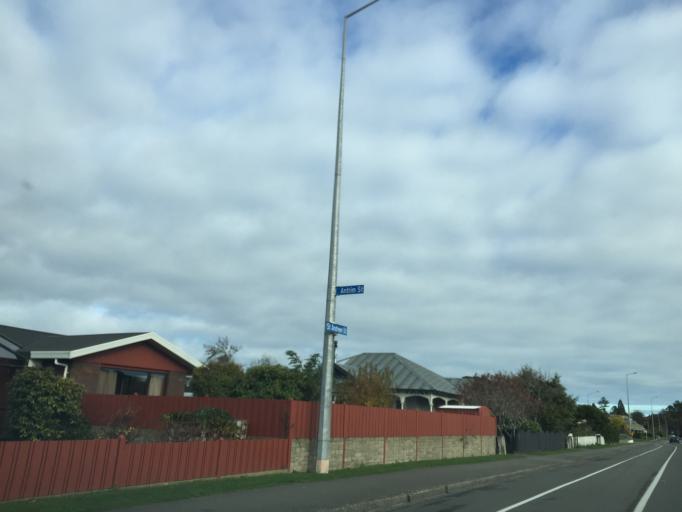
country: NZ
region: Southland
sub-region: Invercargill City
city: Invercargill
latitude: -46.4027
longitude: 168.3665
